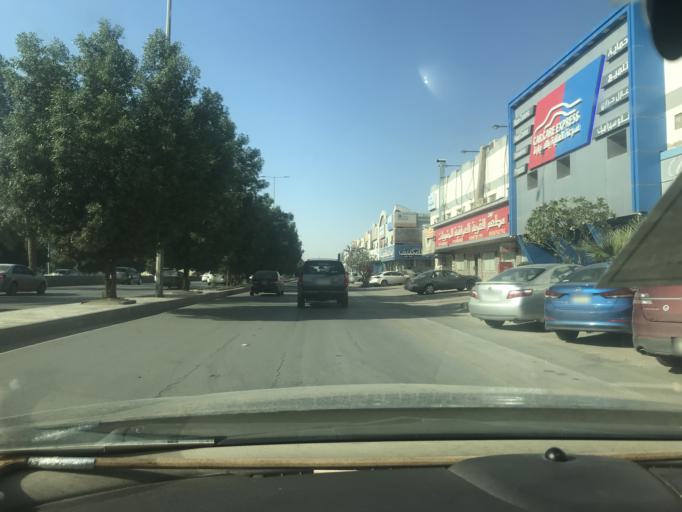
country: SA
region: Ar Riyad
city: Riyadh
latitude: 24.7520
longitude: 46.6727
